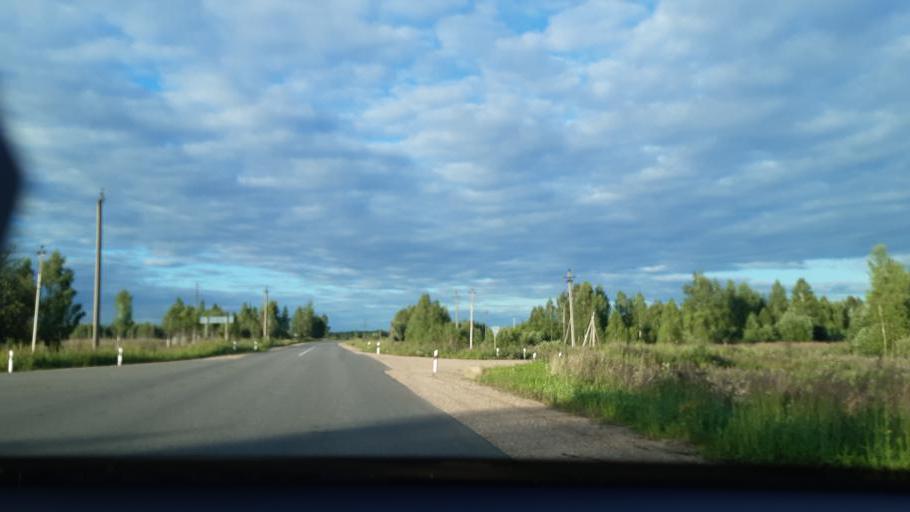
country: RU
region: Smolensk
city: Yel'nya
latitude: 54.5891
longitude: 33.1488
